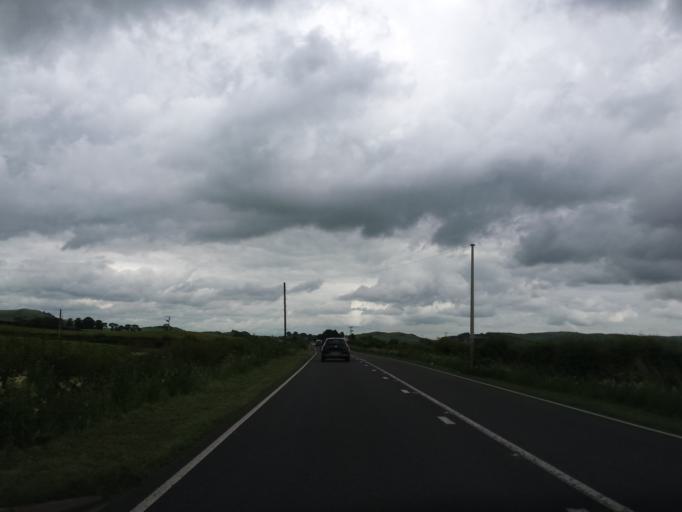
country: GB
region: Scotland
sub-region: Dumfries and Galloway
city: Dalbeattie
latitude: 55.0529
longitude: -3.7515
